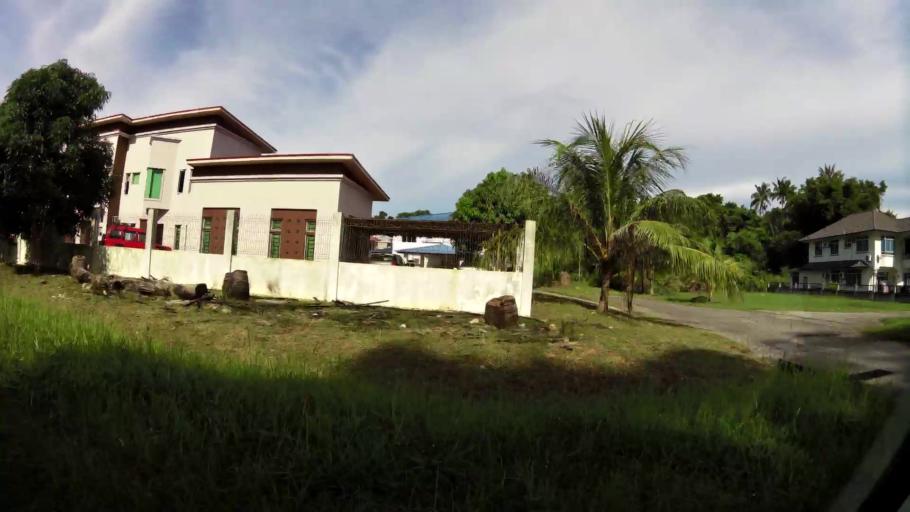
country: BN
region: Brunei and Muara
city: Bandar Seri Begawan
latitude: 4.9849
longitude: 115.0226
